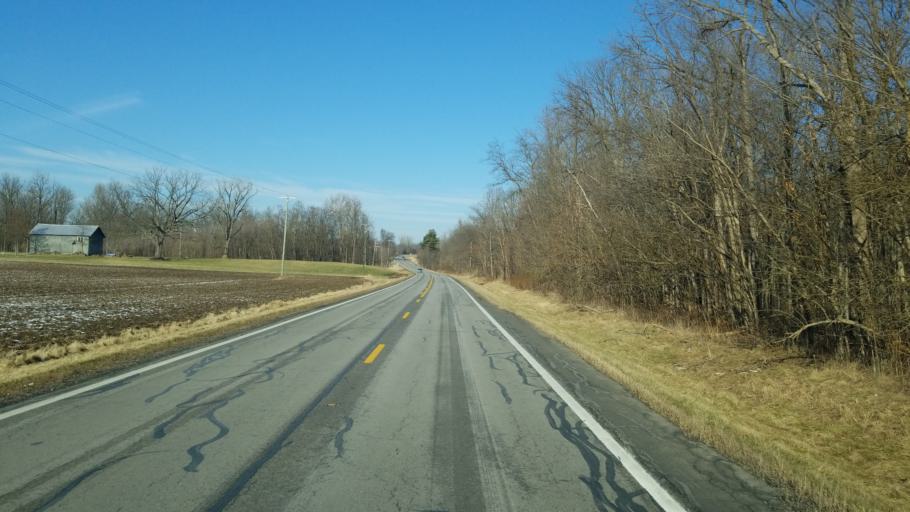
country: US
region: Ohio
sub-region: Huron County
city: Willard
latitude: 41.0956
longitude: -82.6612
